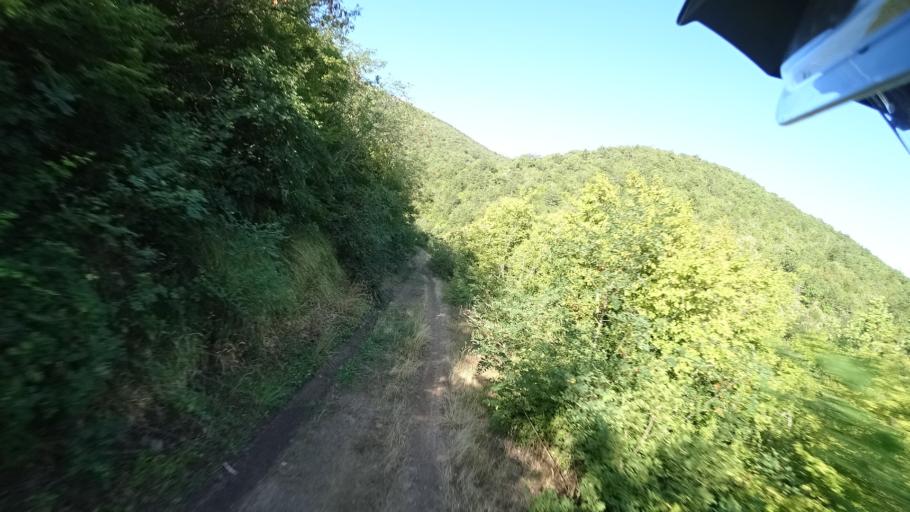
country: HR
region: Sibensko-Kniniska
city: Knin
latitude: 44.1189
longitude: 16.1999
